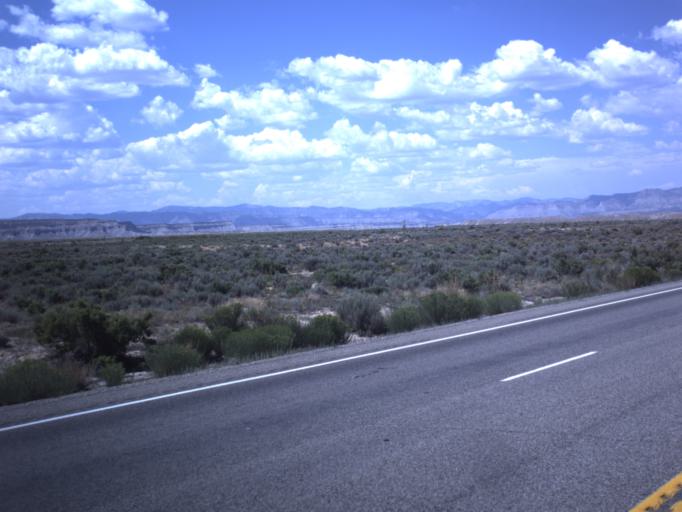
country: US
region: Utah
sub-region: Carbon County
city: Price
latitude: 39.4895
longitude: -110.8480
